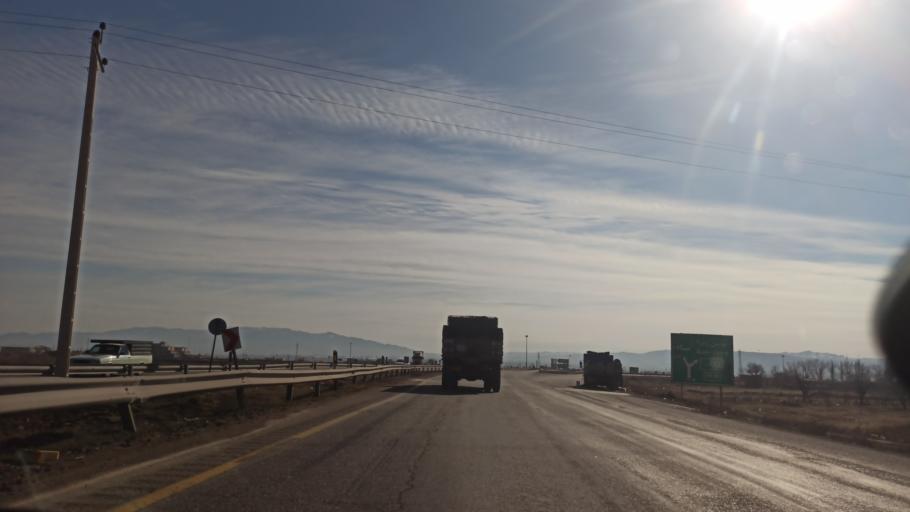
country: IR
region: Qazvin
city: Bu'in Zahra
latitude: 35.7720
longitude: 50.0854
